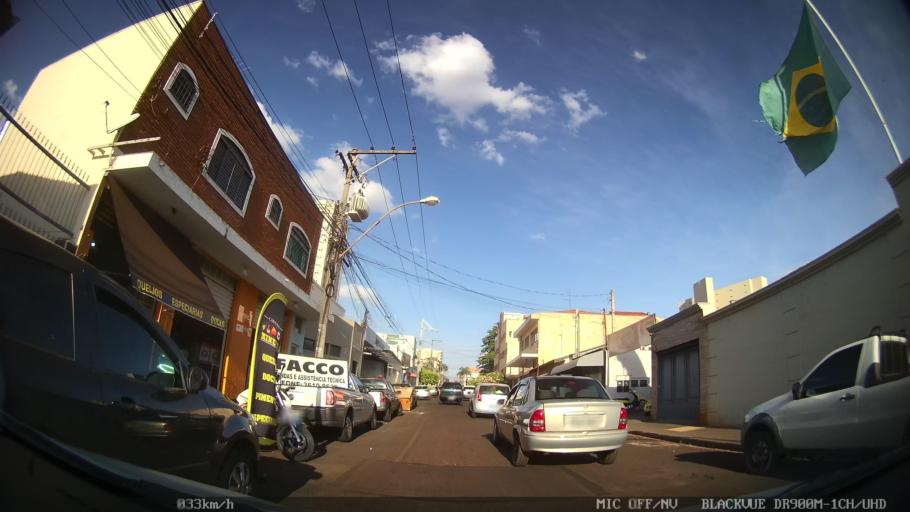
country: BR
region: Sao Paulo
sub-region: Ribeirao Preto
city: Ribeirao Preto
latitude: -21.1823
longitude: -47.7936
